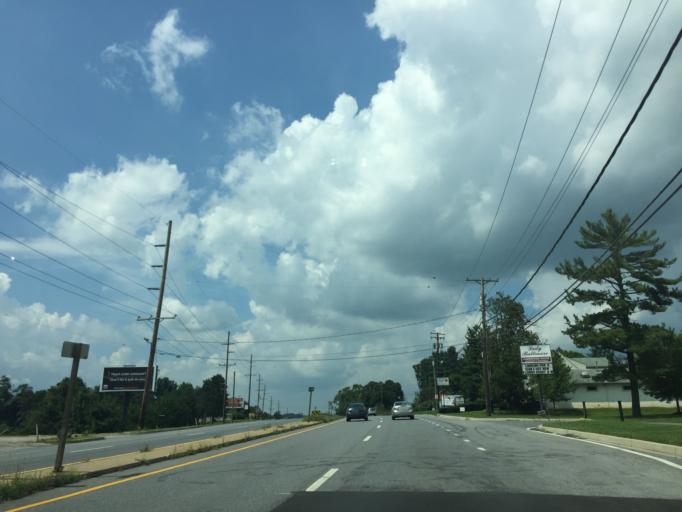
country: US
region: Maryland
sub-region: Baltimore County
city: Reisterstown
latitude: 39.4983
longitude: -76.8938
